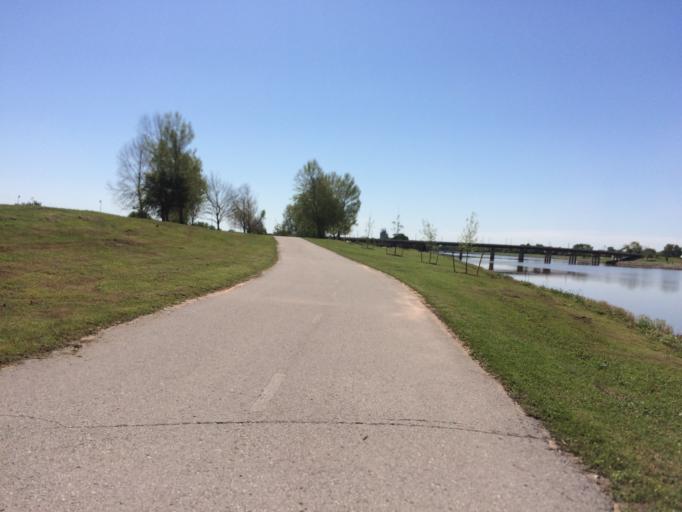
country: US
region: Oklahoma
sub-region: Oklahoma County
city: Oklahoma City
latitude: 35.4559
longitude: -97.5331
